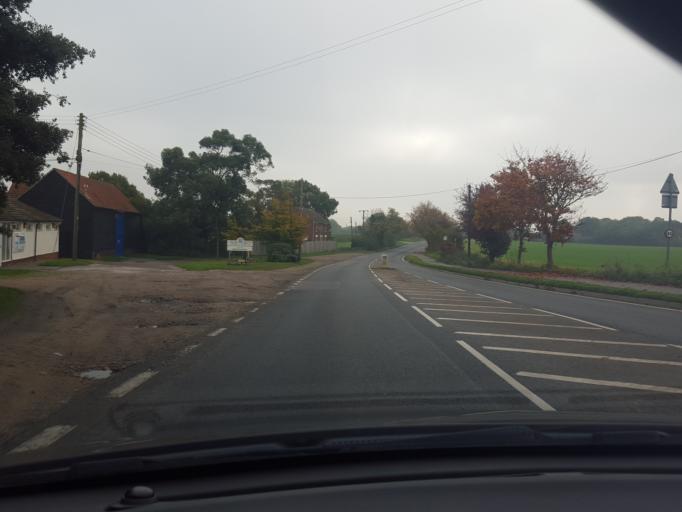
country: GB
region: England
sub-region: Essex
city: Brightlingsea
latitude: 51.8281
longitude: 1.0139
